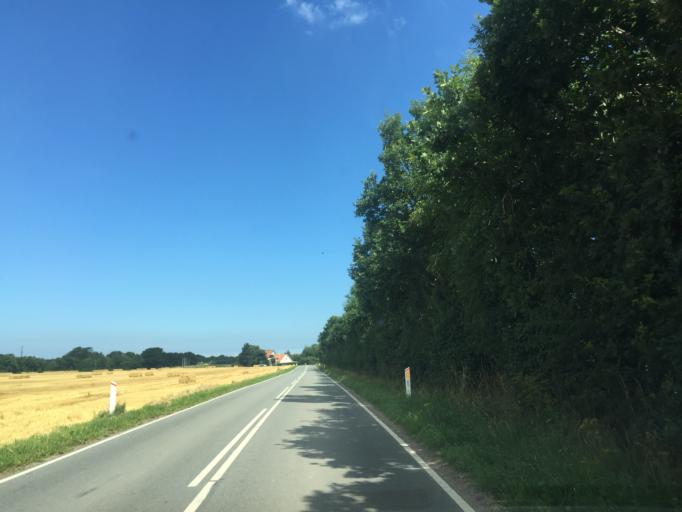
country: DK
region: South Denmark
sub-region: Nordfyns Kommune
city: Otterup
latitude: 55.5626
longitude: 10.3738
